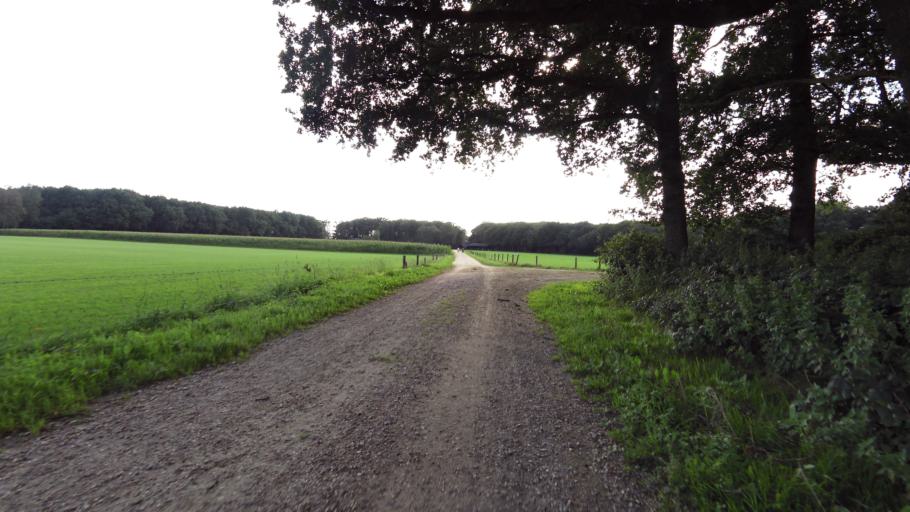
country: NL
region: Gelderland
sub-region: Gemeente Apeldoorn
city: Uddel
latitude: 52.2508
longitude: 5.7789
